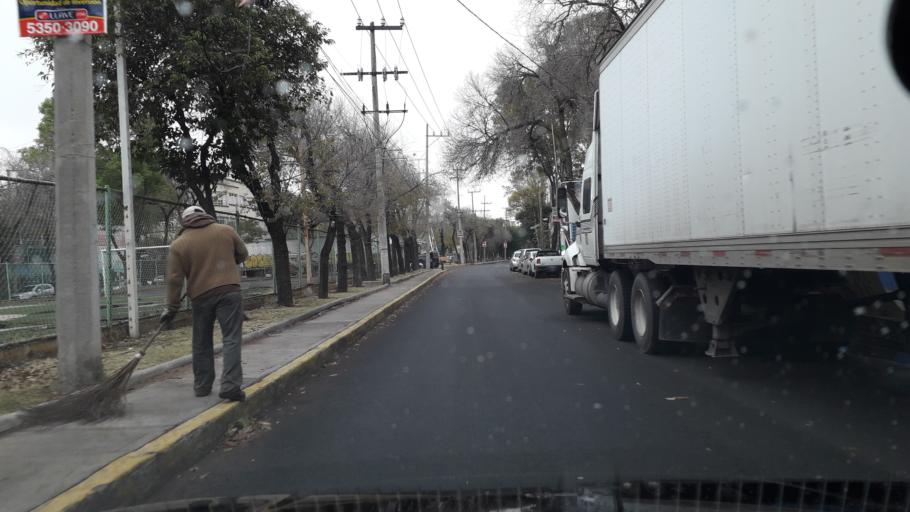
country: MX
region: Mexico City
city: Cuauhtemoc
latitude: 19.4621
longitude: -99.1481
